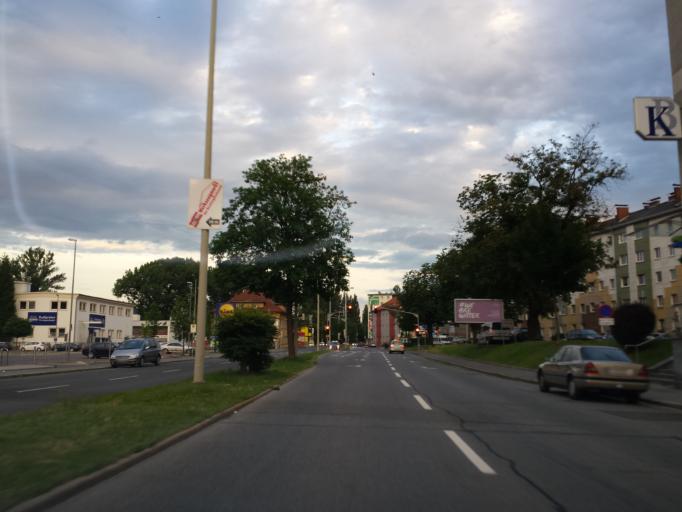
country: AT
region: Styria
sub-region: Graz Stadt
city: Goesting
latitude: 47.0893
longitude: 15.4100
